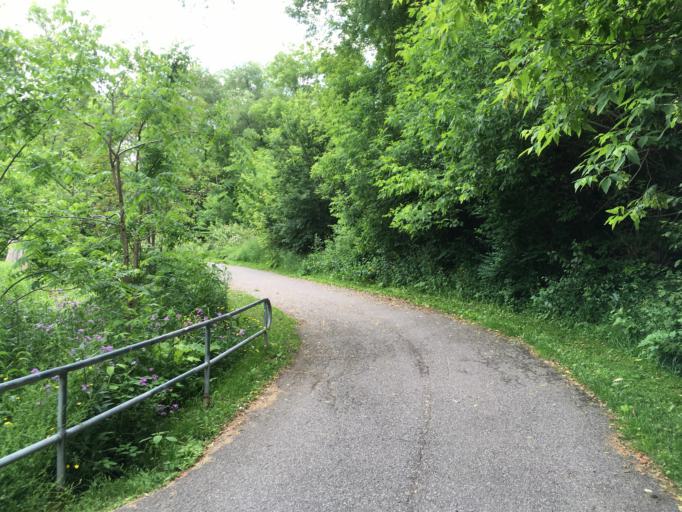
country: CA
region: Ontario
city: Oshawa
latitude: 43.8844
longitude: -78.8629
